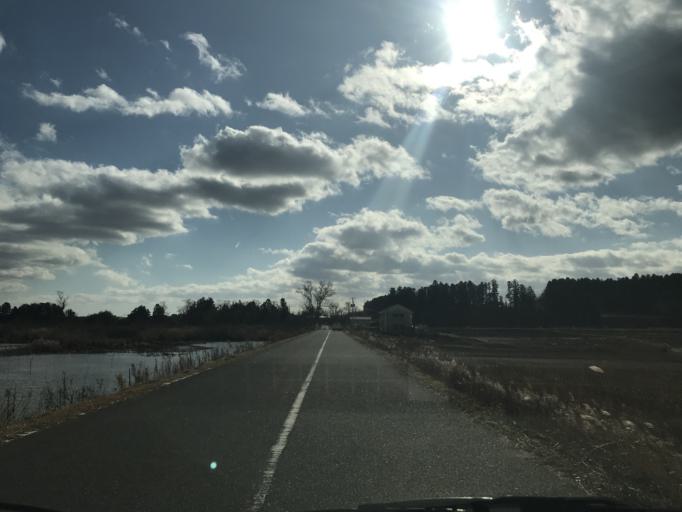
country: JP
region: Miyagi
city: Kogota
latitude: 38.7234
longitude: 141.0757
